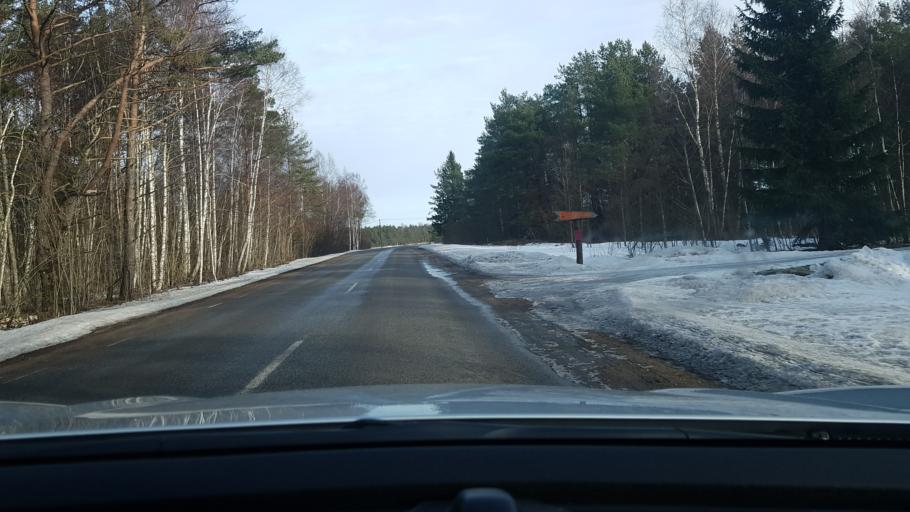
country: EE
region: Saare
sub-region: Kuressaare linn
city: Kuressaare
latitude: 58.3758
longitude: 22.6237
